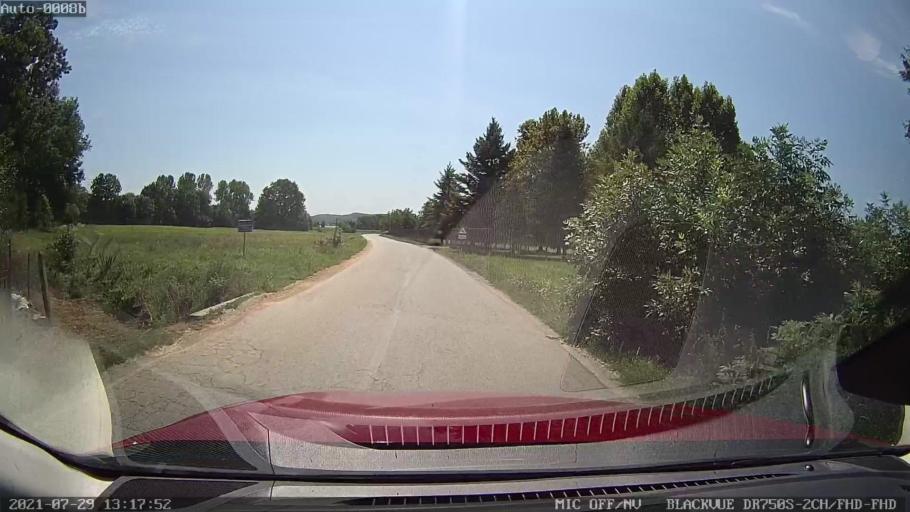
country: HR
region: Varazdinska
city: Varazdin
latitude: 46.2748
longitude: 16.3825
